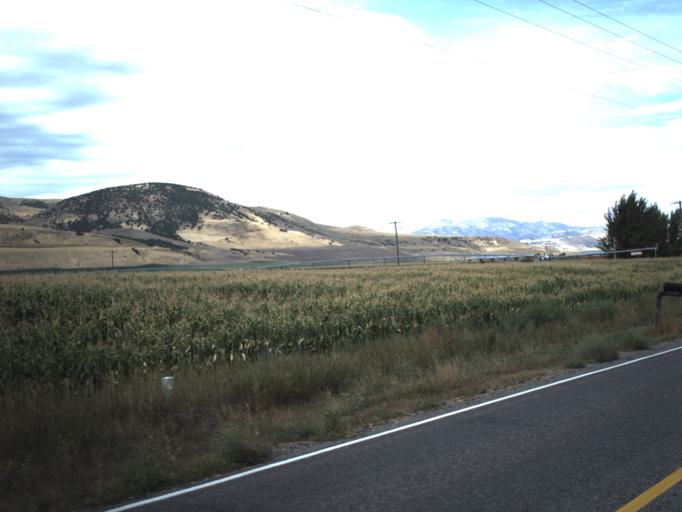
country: US
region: Utah
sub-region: Cache County
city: Lewiston
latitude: 41.9743
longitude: -111.9541
